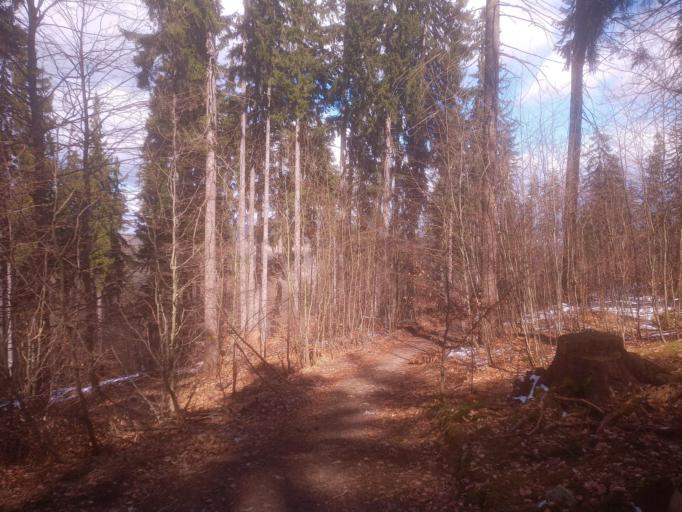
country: PL
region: Lower Silesian Voivodeship
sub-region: Powiat jeleniogorski
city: Szklarska Poreba
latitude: 50.8503
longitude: 15.5480
